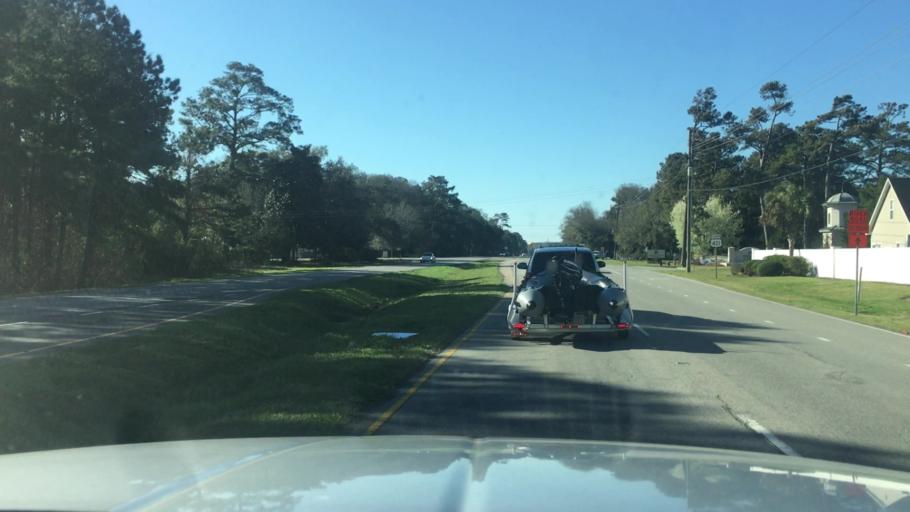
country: US
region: North Carolina
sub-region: New Hanover County
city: Sea Breeze
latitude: 34.0750
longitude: -77.8952
